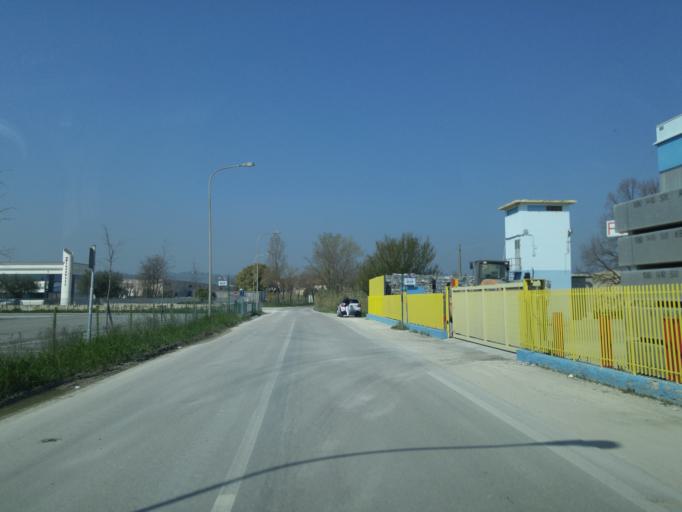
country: IT
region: The Marches
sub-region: Provincia di Pesaro e Urbino
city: Bellocchi
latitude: 43.7897
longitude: 13.0091
